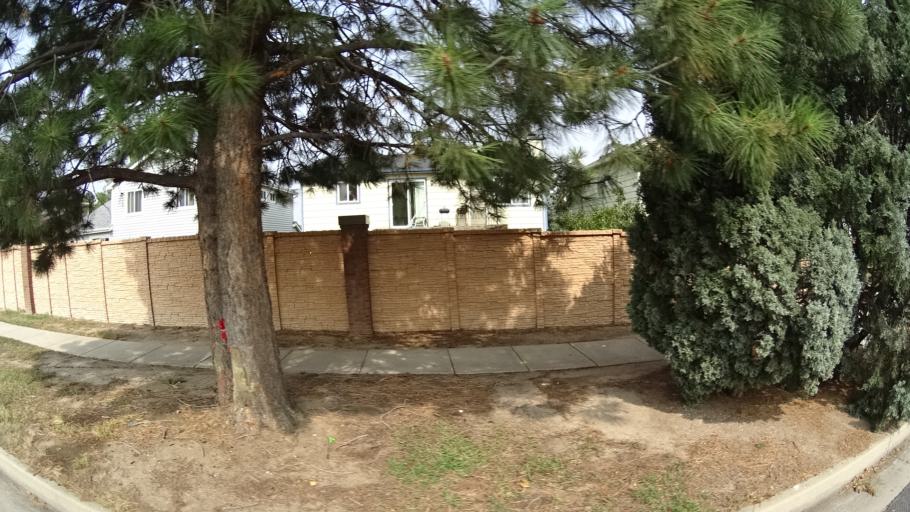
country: US
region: Colorado
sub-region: El Paso County
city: Cimarron Hills
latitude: 38.9171
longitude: -104.7277
